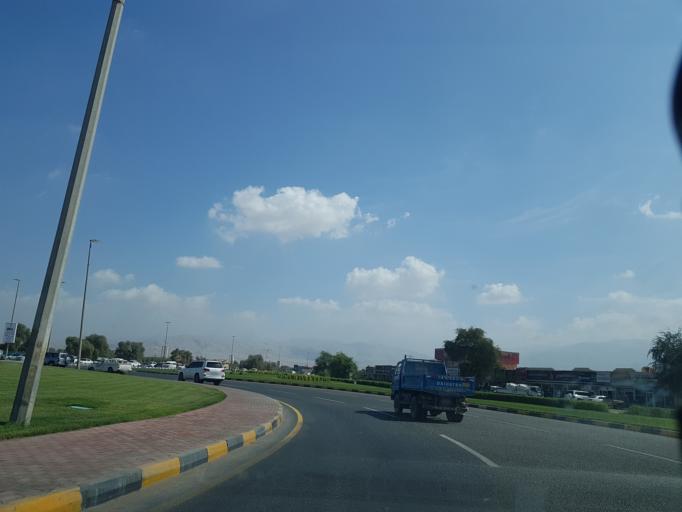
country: AE
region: Ra's al Khaymah
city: Ras al-Khaimah
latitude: 25.7130
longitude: 55.9709
